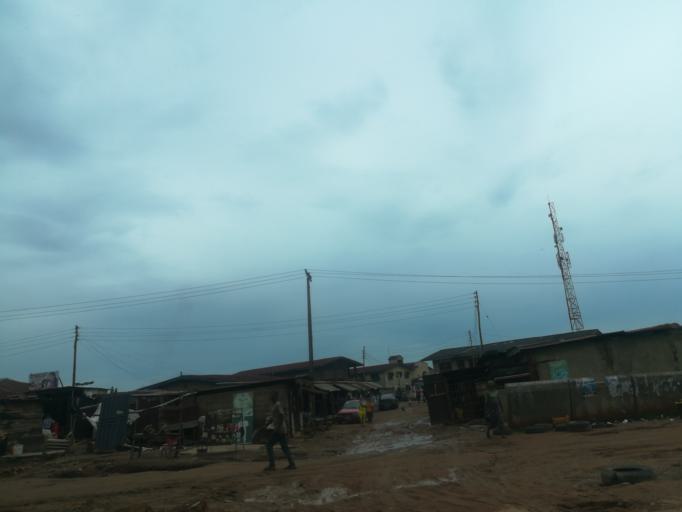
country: NG
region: Oyo
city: Ibadan
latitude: 7.3922
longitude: 3.9588
